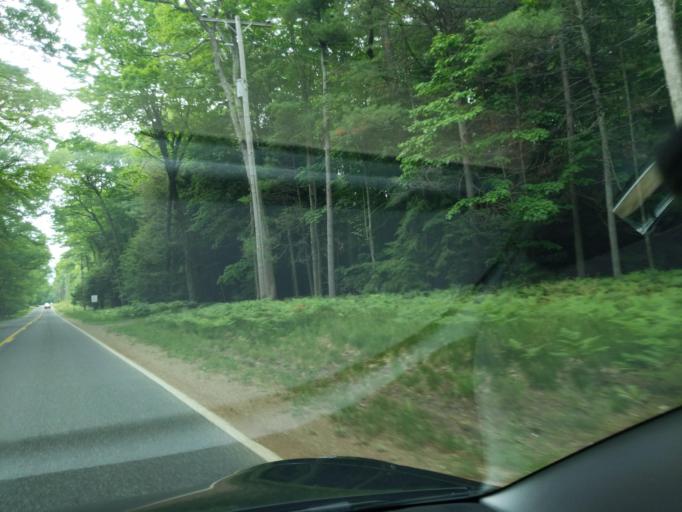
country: US
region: Michigan
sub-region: Muskegon County
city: Whitehall
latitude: 43.2997
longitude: -86.3784
